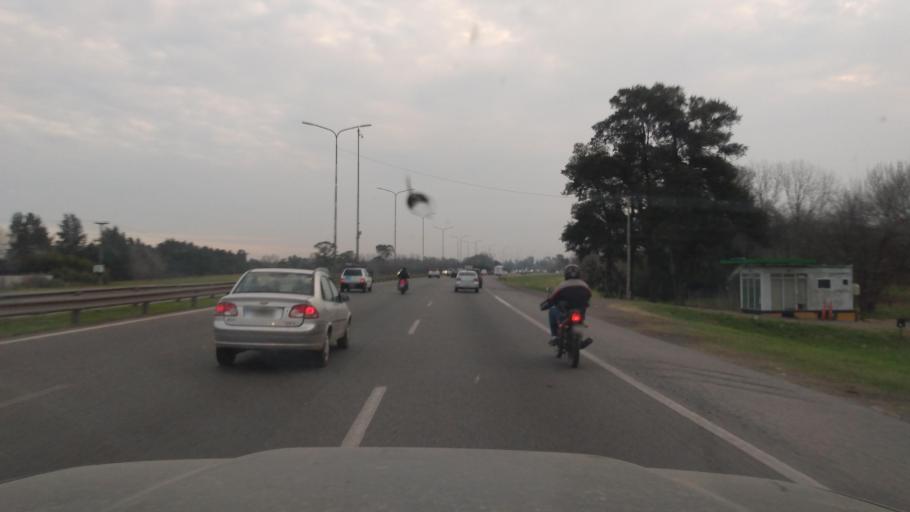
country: AR
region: Buenos Aires
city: Hurlingham
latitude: -34.6006
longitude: -58.6985
